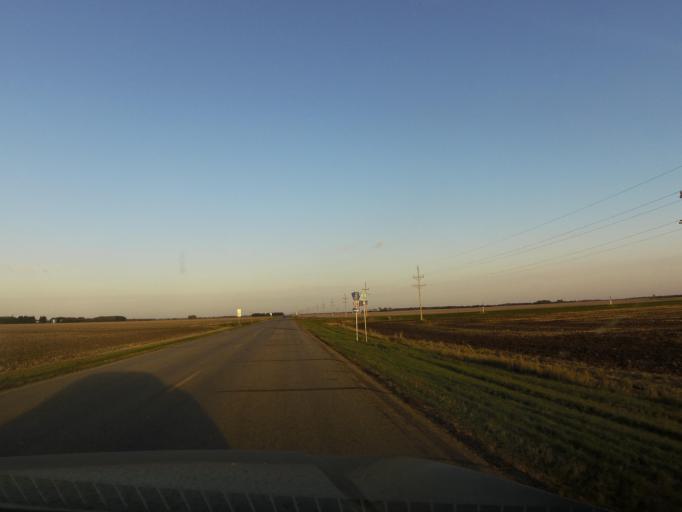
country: CA
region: Manitoba
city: Altona
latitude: 48.9635
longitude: -97.6254
